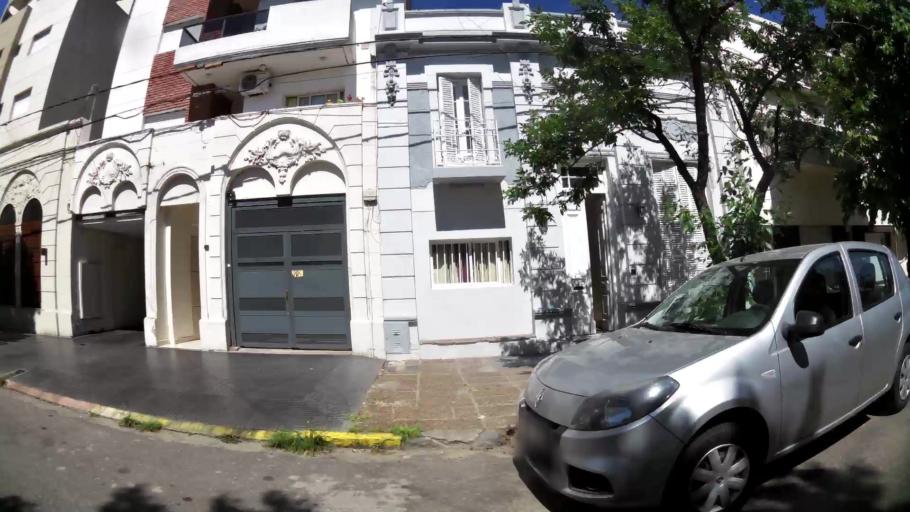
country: AR
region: Santa Fe
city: Santa Fe de la Vera Cruz
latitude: -31.6401
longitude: -60.6884
